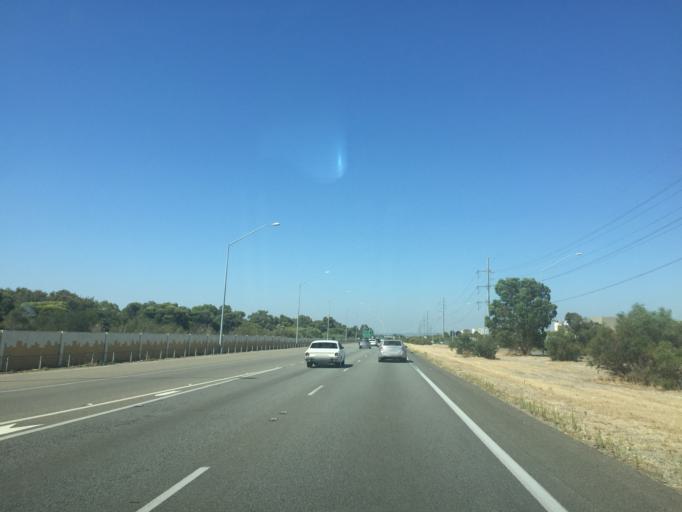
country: AU
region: Western Australia
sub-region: Canning
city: Willetton
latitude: -32.0653
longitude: 115.8943
